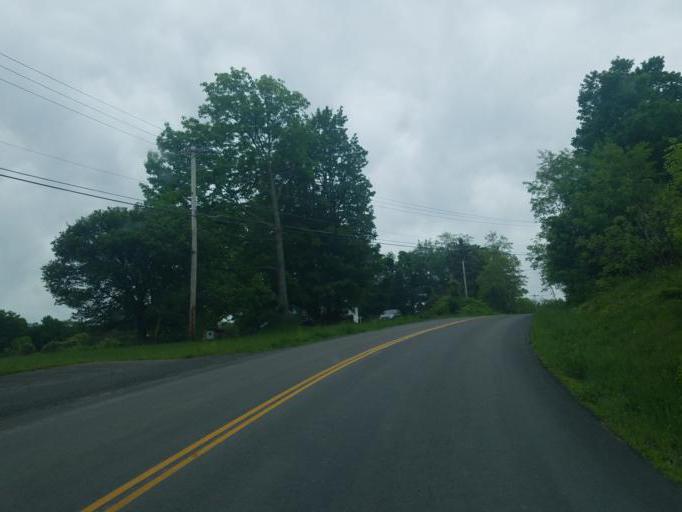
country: US
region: New York
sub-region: Herkimer County
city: Ilion
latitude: 42.9757
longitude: -75.0258
